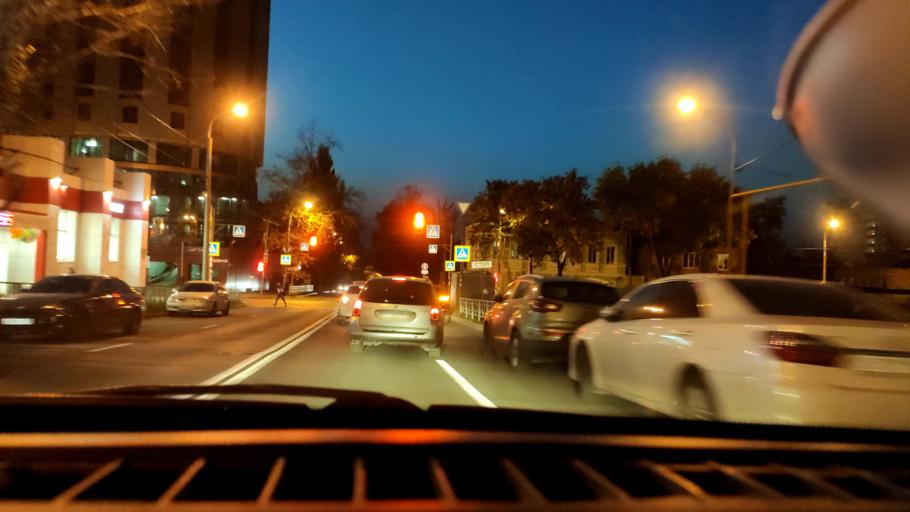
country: RU
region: Samara
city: Rozhdestveno
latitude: 53.1843
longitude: 50.0808
